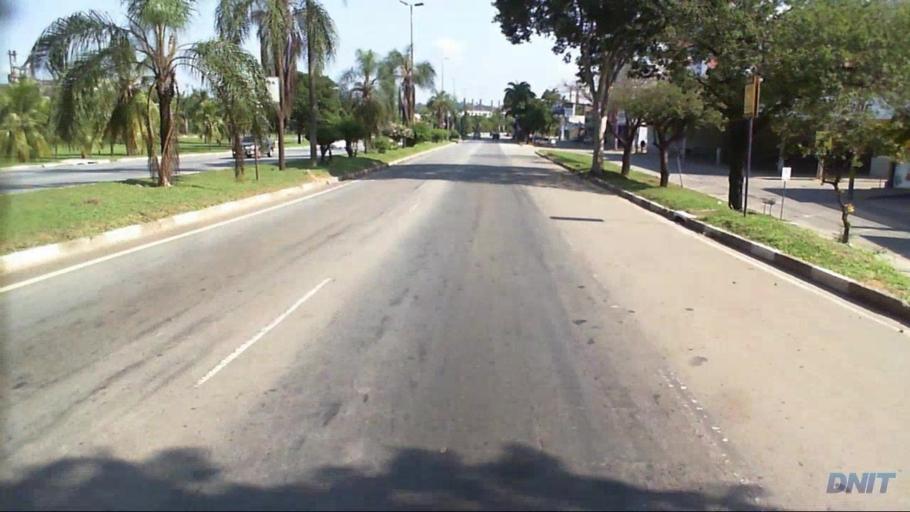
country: BR
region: Minas Gerais
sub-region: Ipatinga
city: Ipatinga
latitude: -19.4788
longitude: -42.5444
